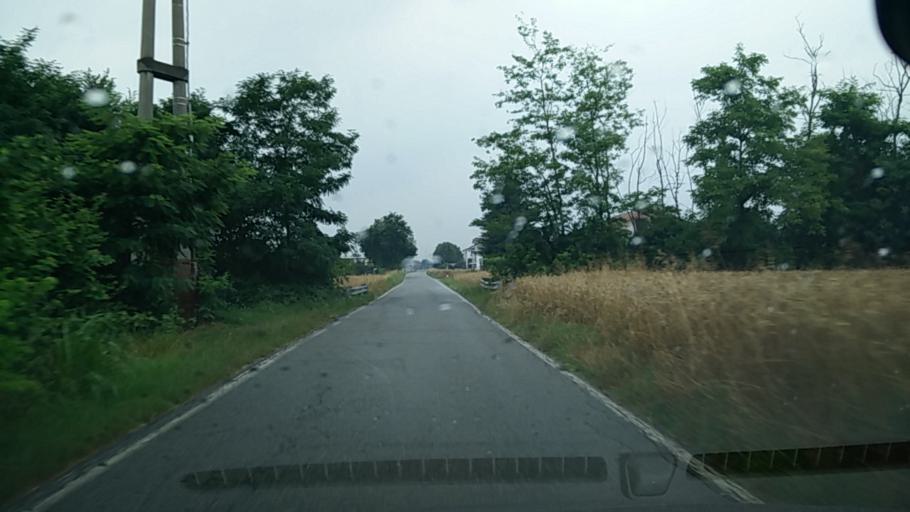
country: IT
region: Piedmont
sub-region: Provincia di Torino
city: Leini
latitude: 45.2010
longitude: 7.7323
